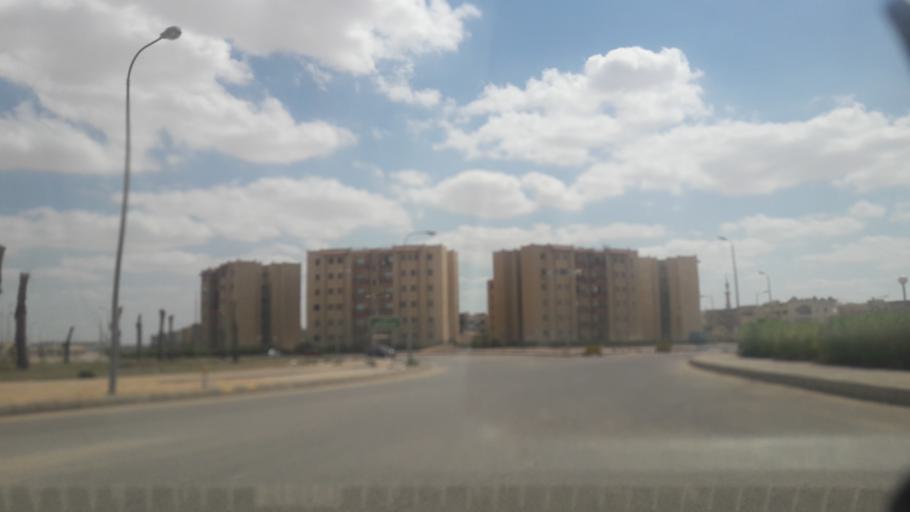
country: EG
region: Al Jizah
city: Madinat Sittah Uktubar
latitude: 29.9355
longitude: 31.0653
